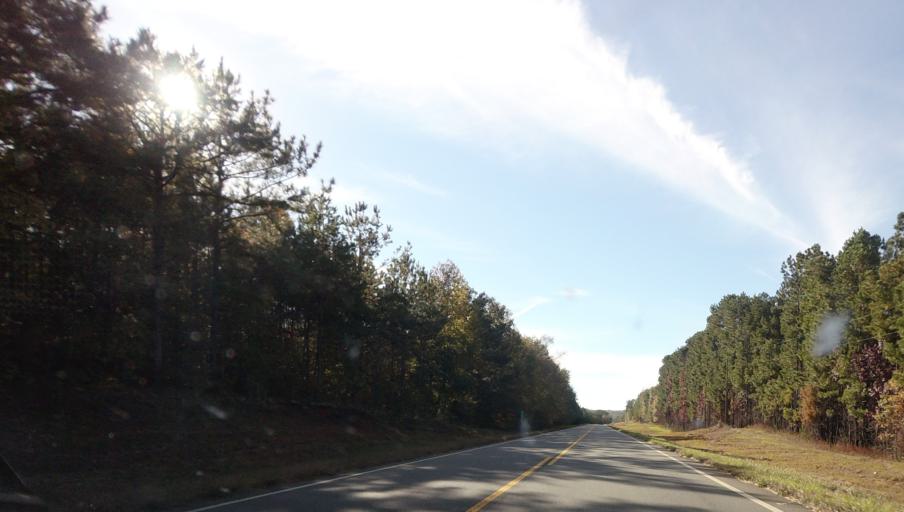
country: US
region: Georgia
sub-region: Talbot County
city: Talbotton
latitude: 32.6889
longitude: -84.4994
